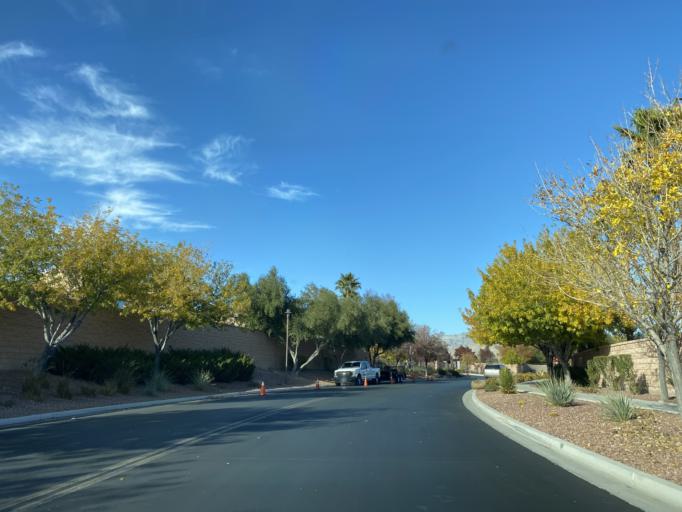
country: US
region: Nevada
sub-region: Clark County
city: North Las Vegas
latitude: 36.3165
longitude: -115.2569
